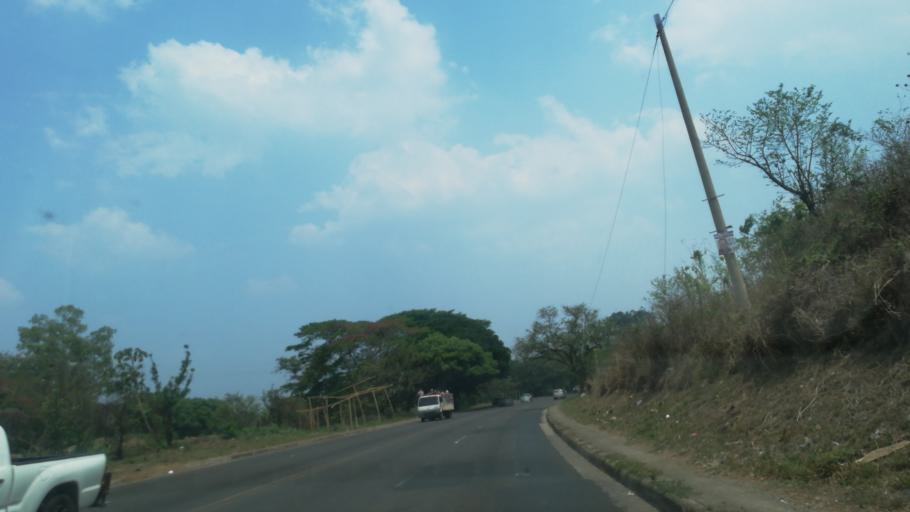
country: SV
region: Santa Ana
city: Santa Ana
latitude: 13.9787
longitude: -89.5948
